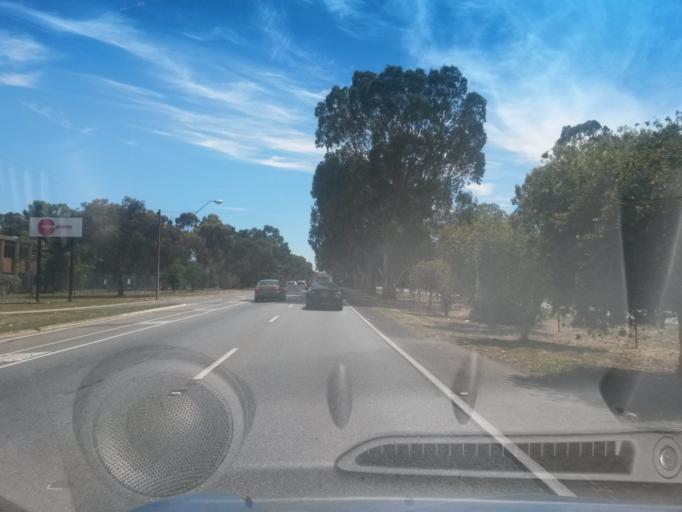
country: AU
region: South Australia
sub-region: Salisbury
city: Salisbury
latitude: -34.7859
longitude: 138.6518
